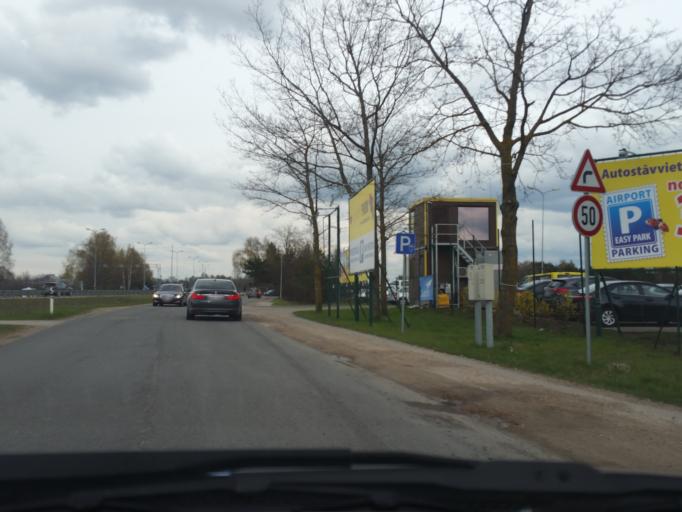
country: LV
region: Marupe
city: Marupe
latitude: 56.9216
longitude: 23.9937
